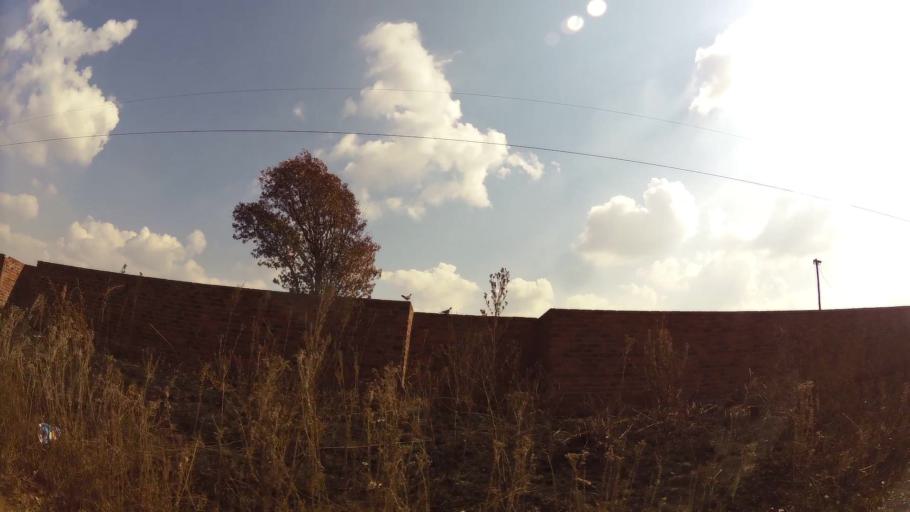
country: ZA
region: Mpumalanga
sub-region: Nkangala District Municipality
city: Delmas
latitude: -26.1700
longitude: 28.5460
